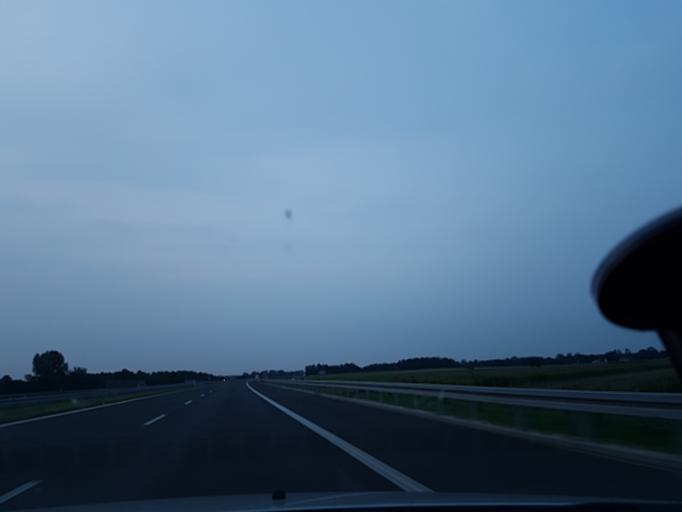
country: PL
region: Lodz Voivodeship
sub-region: Powiat zgierski
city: Strykow
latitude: 51.9510
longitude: 19.6032
